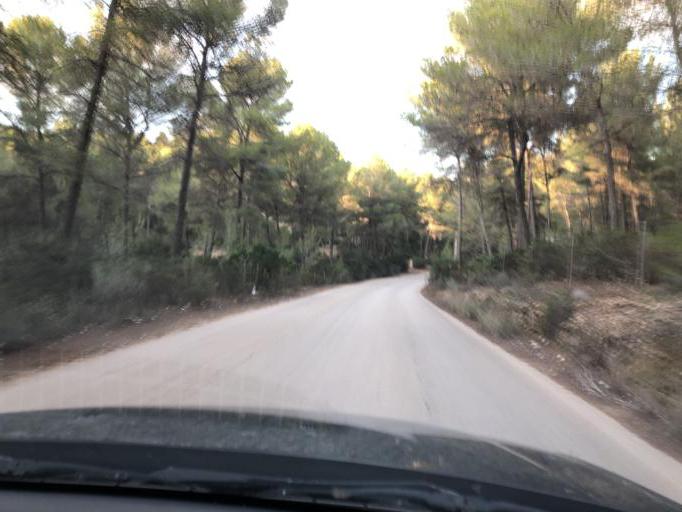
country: ES
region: Balearic Islands
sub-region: Illes Balears
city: Santa Ponsa
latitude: 39.5367
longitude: 2.4815
